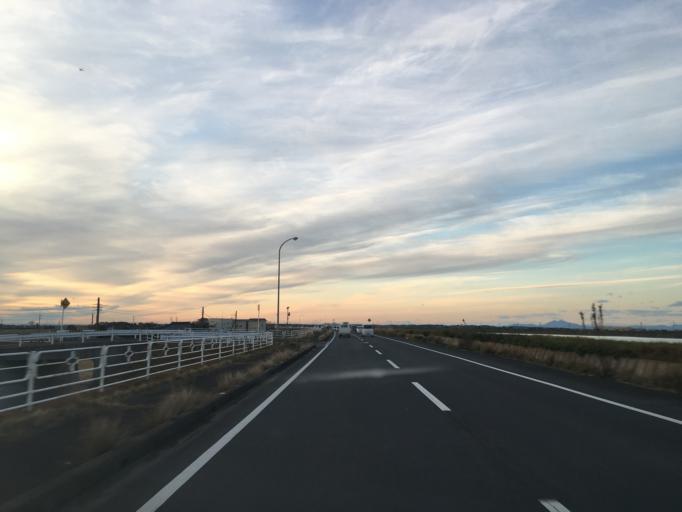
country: JP
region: Chiba
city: Katori-shi
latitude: 35.9131
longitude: 140.4717
